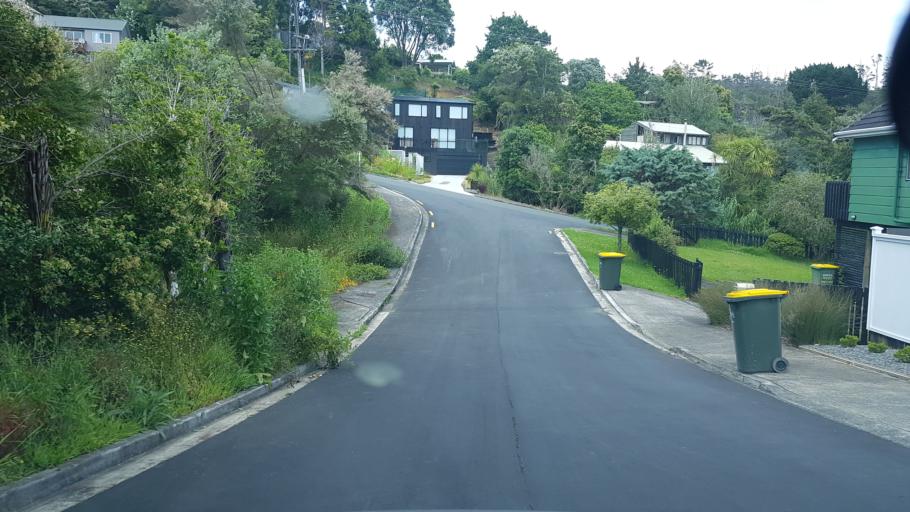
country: NZ
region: Auckland
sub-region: Auckland
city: North Shore
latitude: -36.8136
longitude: 174.7032
